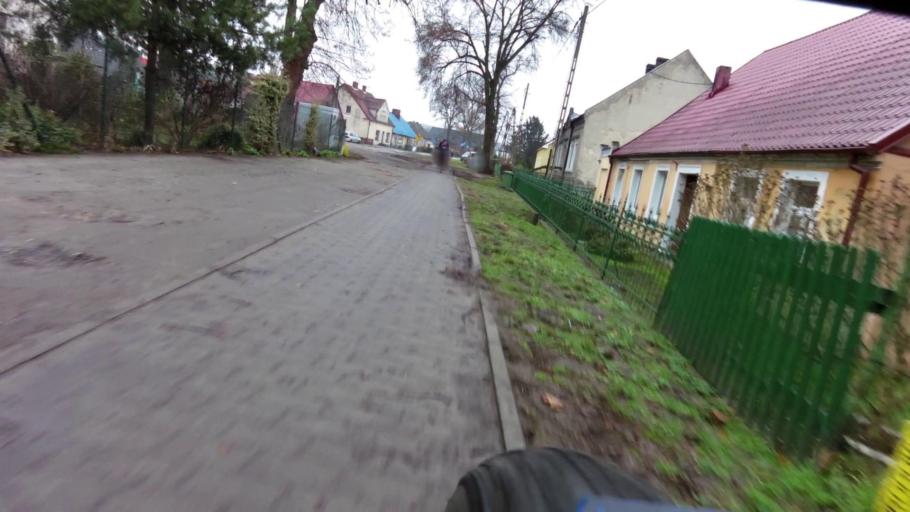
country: PL
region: Lubusz
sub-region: Powiat gorzowski
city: Kostrzyn nad Odra
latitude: 52.6202
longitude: 14.7067
